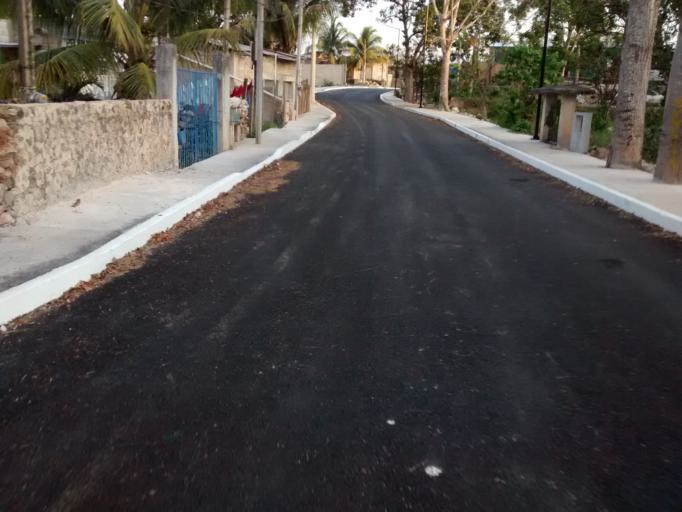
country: MX
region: Yucatan
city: Valladolid
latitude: 20.6827
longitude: -88.1933
